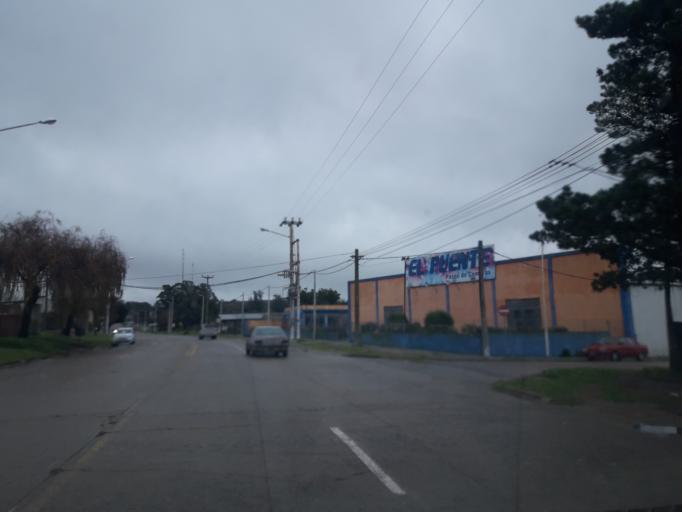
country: AR
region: Buenos Aires
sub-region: Partido de Tandil
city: Tandil
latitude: -37.3206
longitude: -59.1638
